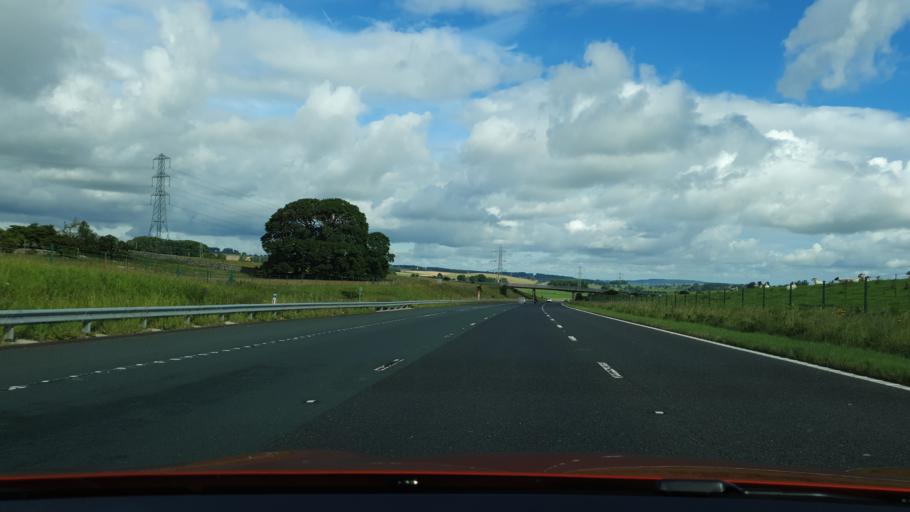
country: GB
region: England
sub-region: Cumbria
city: Penrith
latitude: 54.5442
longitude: -2.6670
